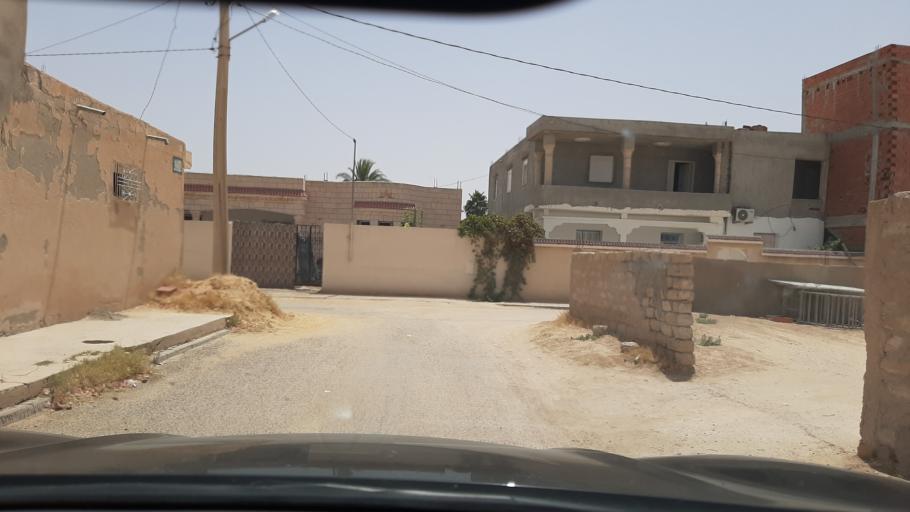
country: TN
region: Qabis
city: Matmata
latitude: 33.6167
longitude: 10.2782
